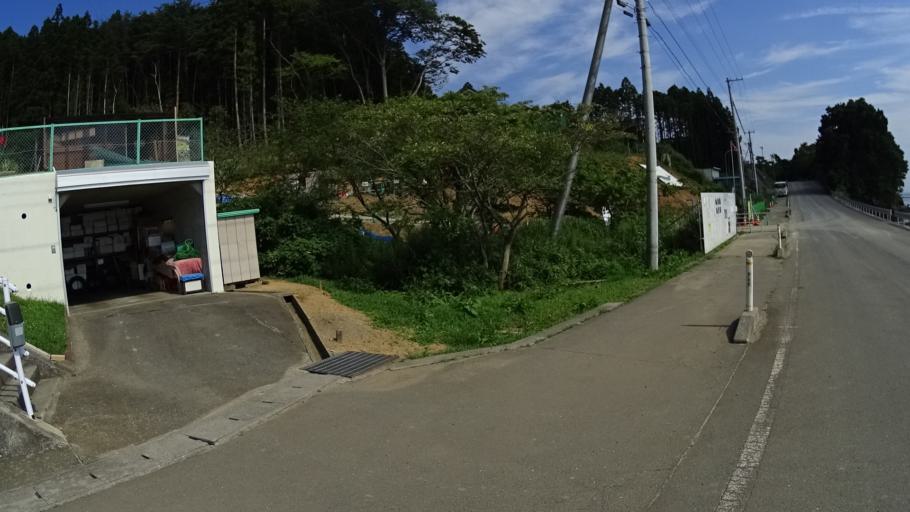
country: JP
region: Iwate
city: Ofunato
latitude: 38.8724
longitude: 141.6026
